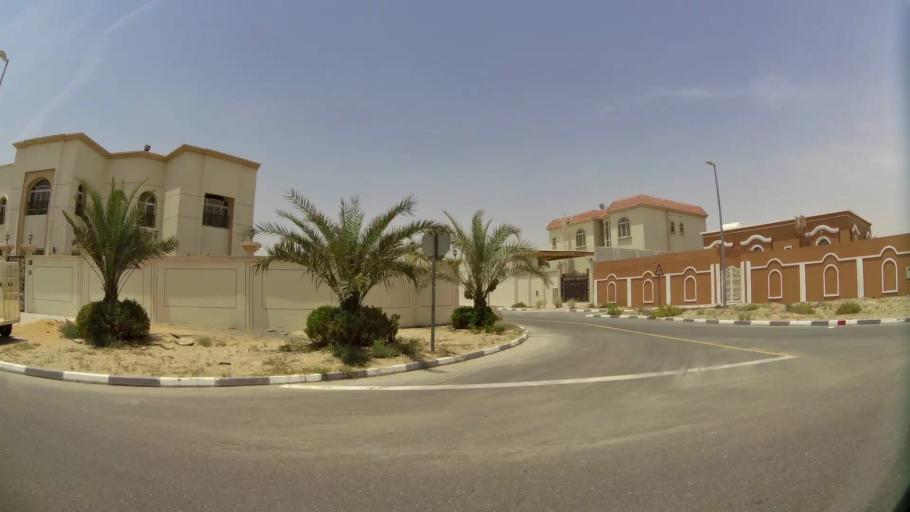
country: AE
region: Ash Shariqah
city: Sharjah
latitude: 25.2503
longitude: 55.4679
